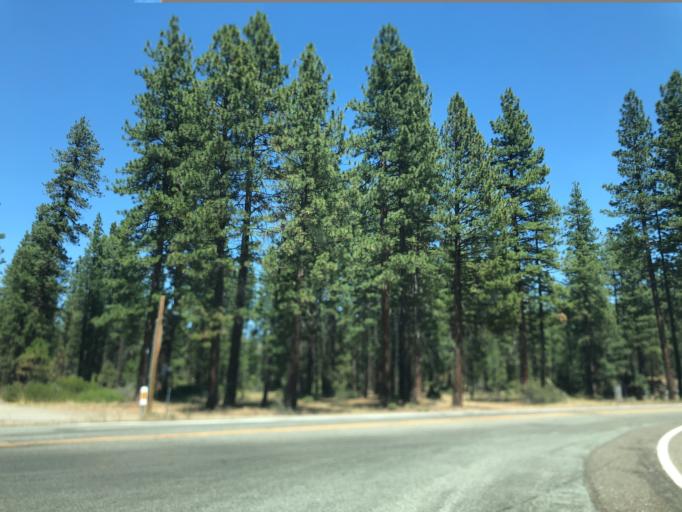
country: US
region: California
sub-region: Shasta County
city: Burney
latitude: 40.6805
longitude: -121.4246
